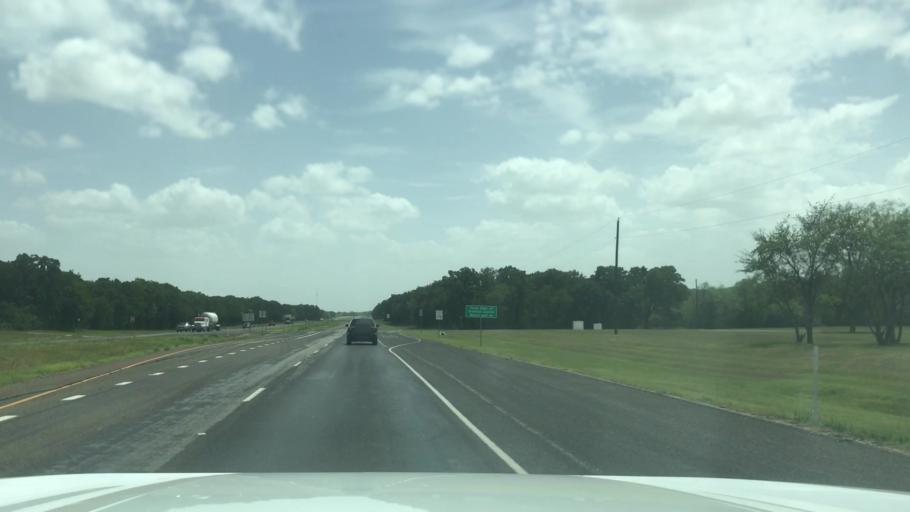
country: US
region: Texas
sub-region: Falls County
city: Marlin
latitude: 31.2994
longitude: -96.8750
